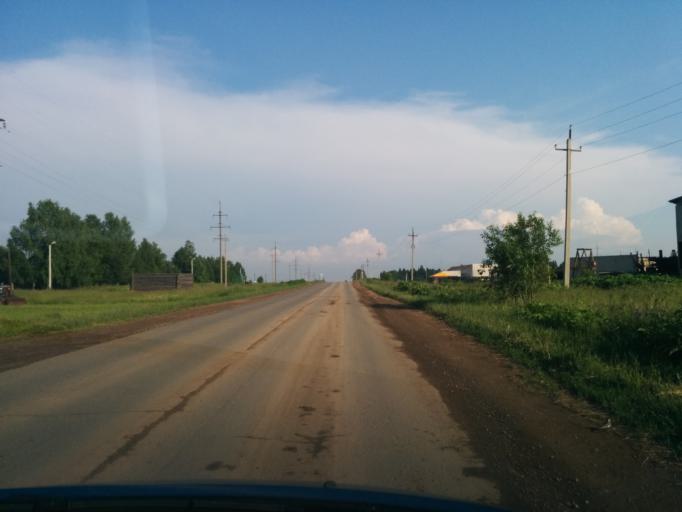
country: RU
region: Perm
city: Polazna
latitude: 58.2290
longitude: 56.2900
